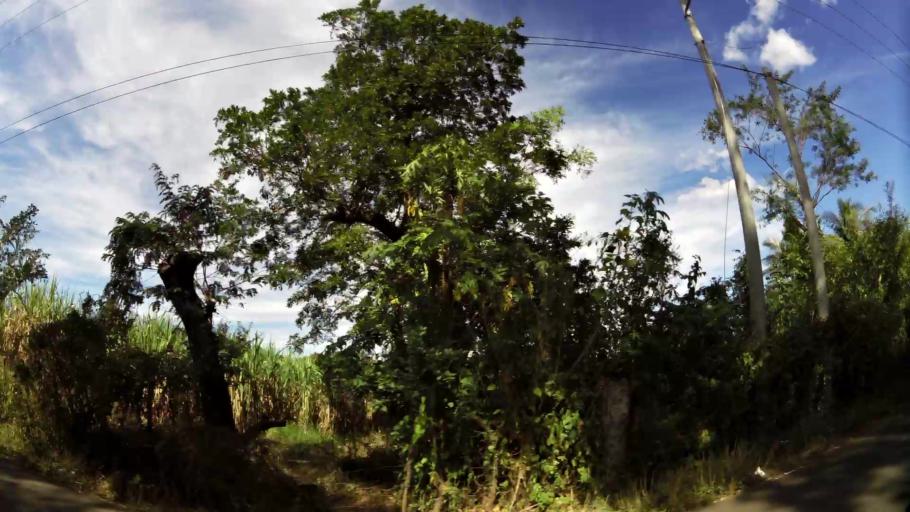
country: SV
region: San Salvador
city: Aguilares
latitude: 13.9572
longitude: -89.1459
